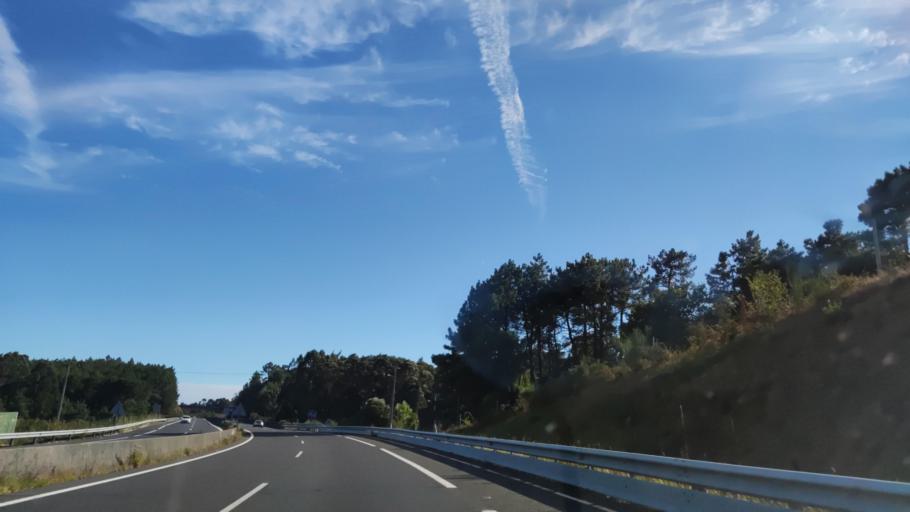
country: ES
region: Galicia
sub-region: Provincia da Coruna
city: Boiro
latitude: 42.6431
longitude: -8.9113
